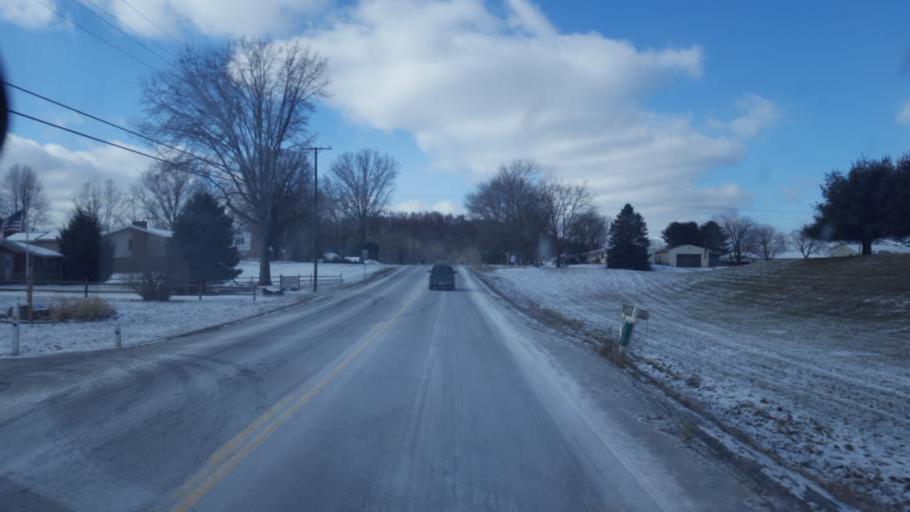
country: US
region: Ohio
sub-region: Coshocton County
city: Coshocton
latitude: 40.3029
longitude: -81.9110
